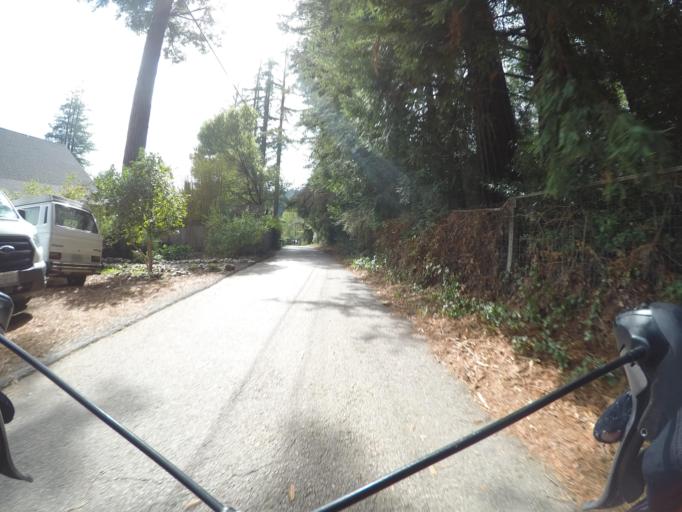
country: US
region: California
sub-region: Santa Cruz County
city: Ben Lomond
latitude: 37.0930
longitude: -122.0919
